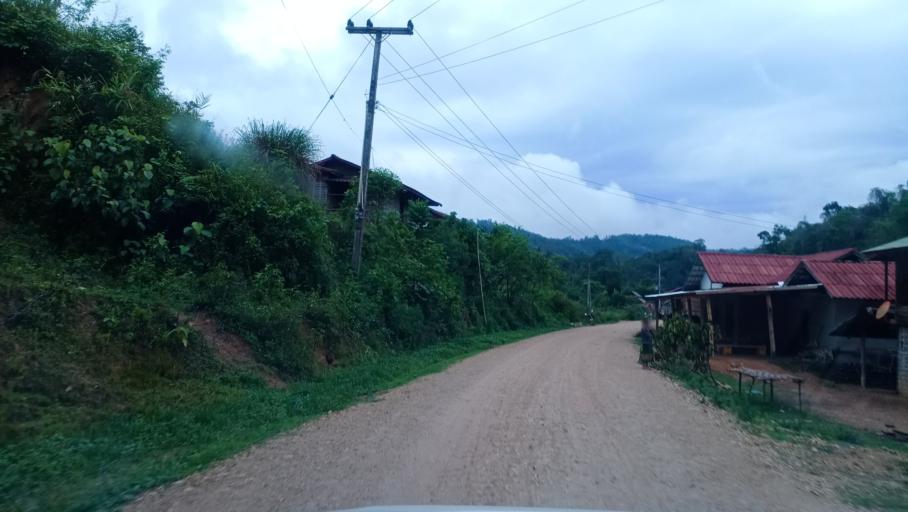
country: LA
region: Phongsali
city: Khoa
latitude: 21.2561
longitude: 102.6980
